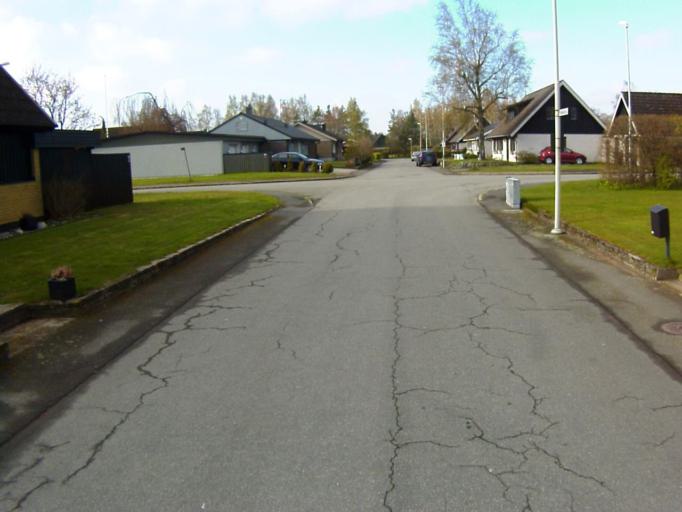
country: SE
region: Skane
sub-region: Kristianstads Kommun
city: Kristianstad
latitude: 56.0144
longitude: 14.1059
